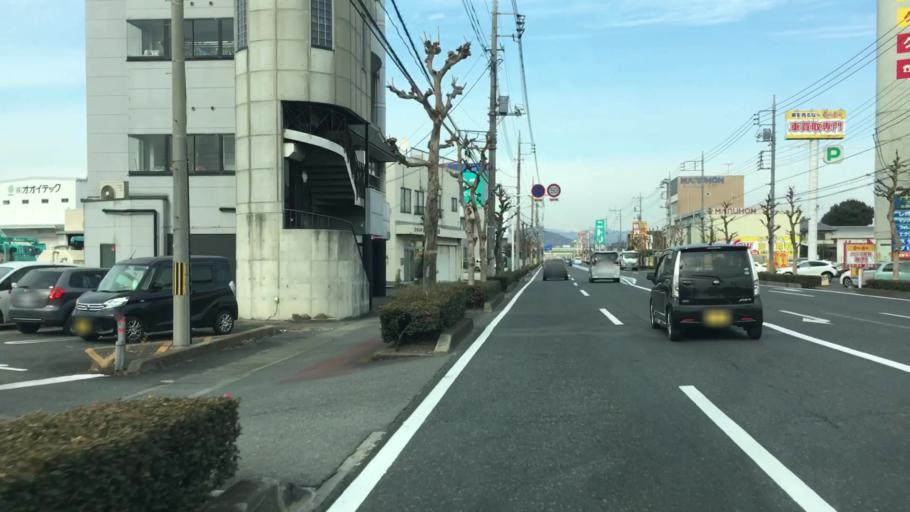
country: JP
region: Gunma
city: Ota
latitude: 36.2635
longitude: 139.3769
